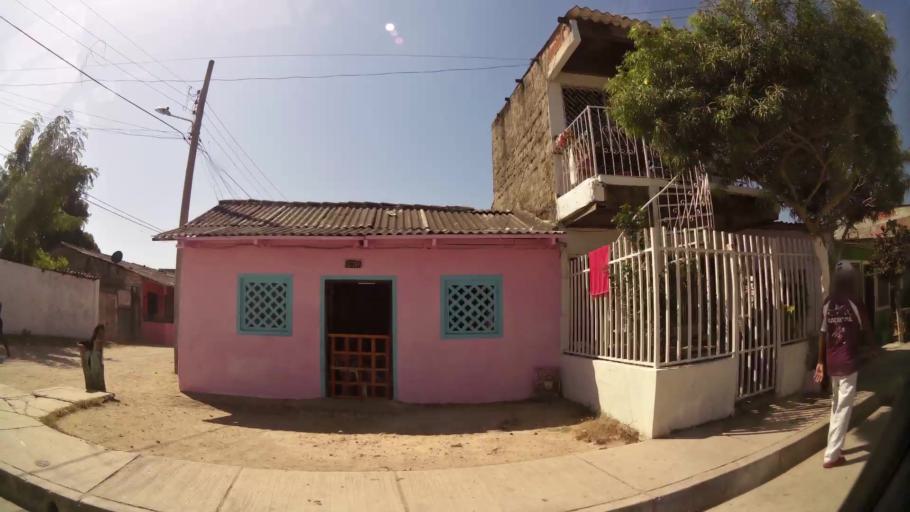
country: CO
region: Bolivar
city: Cartagena
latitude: 10.4411
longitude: -75.5165
